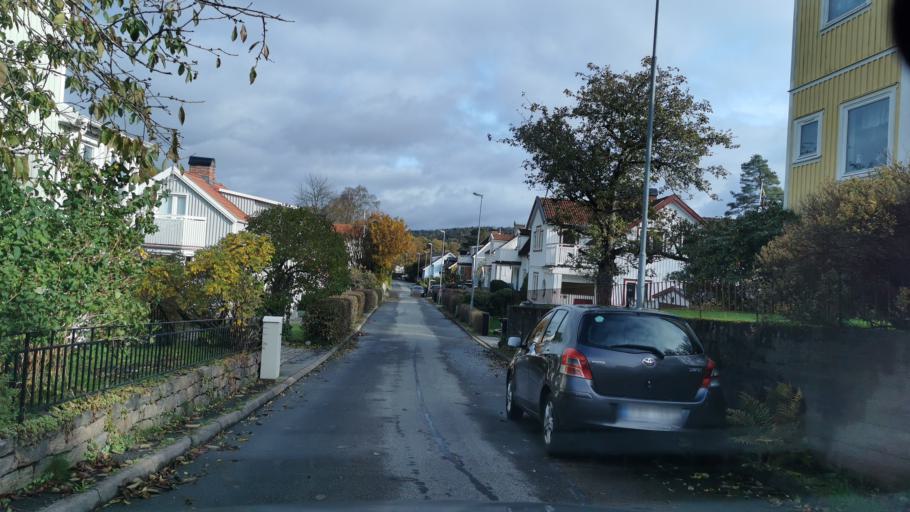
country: SE
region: Vaestra Goetaland
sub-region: Partille Kommun
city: Partille
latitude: 57.7268
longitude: 12.0740
